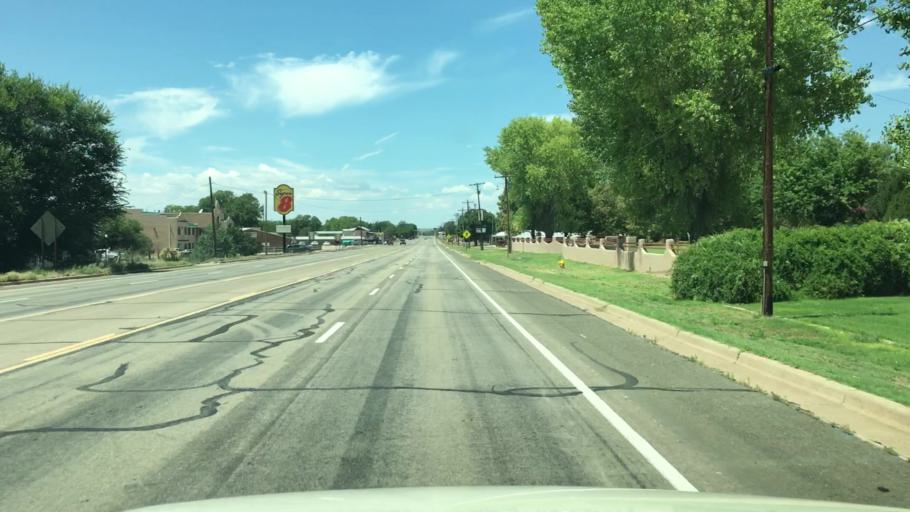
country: US
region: New Mexico
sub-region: De Baca County
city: Fort Sumner
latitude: 34.4655
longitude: -104.2257
